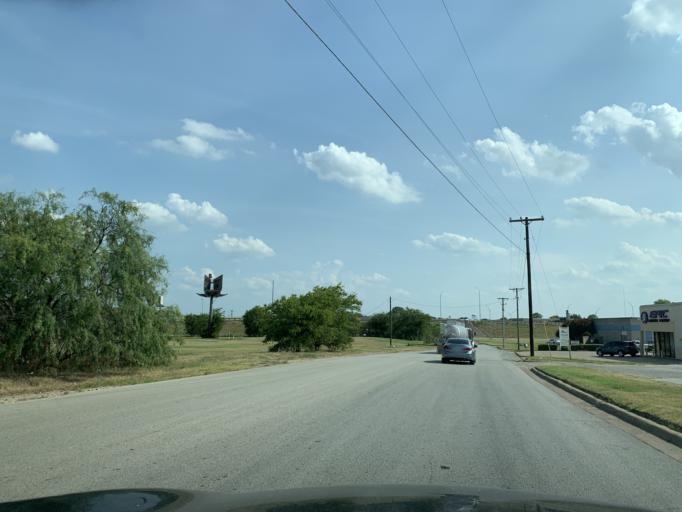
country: US
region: Texas
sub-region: Tarrant County
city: Haltom City
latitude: 32.7944
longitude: -97.2442
